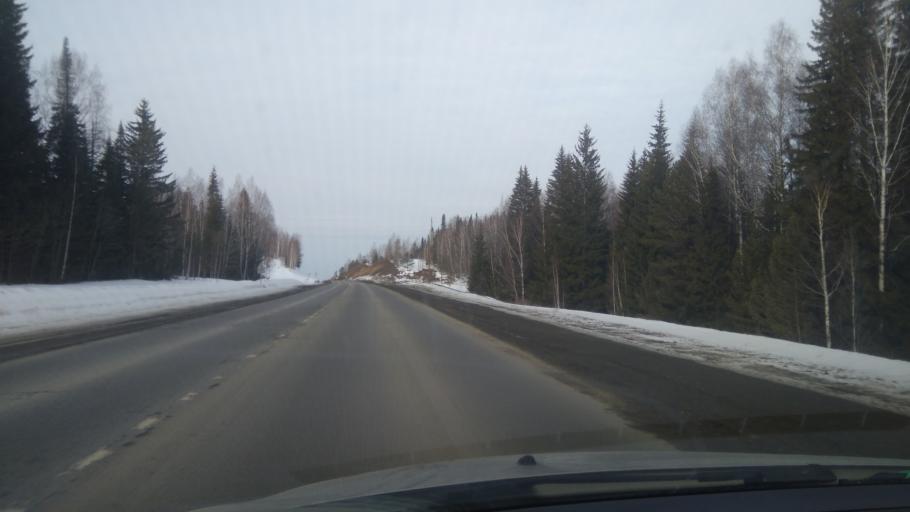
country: RU
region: Sverdlovsk
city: Bisert'
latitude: 56.8296
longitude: 59.0858
